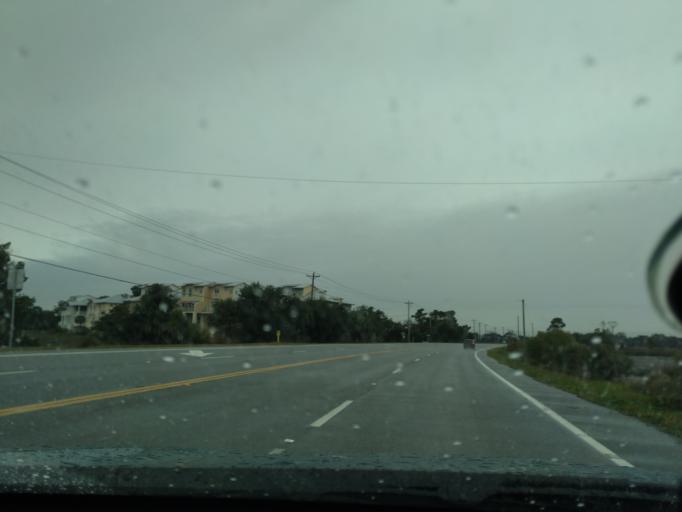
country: US
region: South Carolina
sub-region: Charleston County
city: Folly Beach
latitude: 32.6779
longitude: -79.9532
